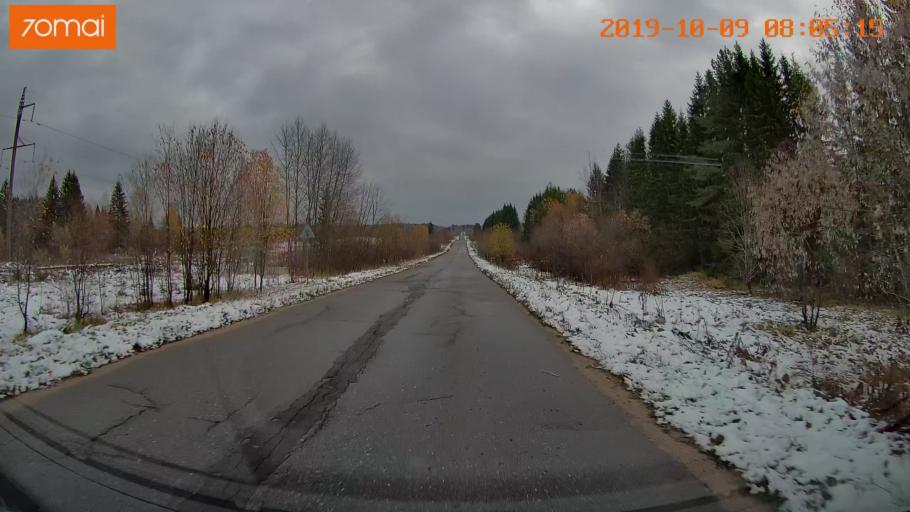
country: RU
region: Jaroslavl
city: Kukoboy
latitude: 58.6905
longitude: 40.0405
